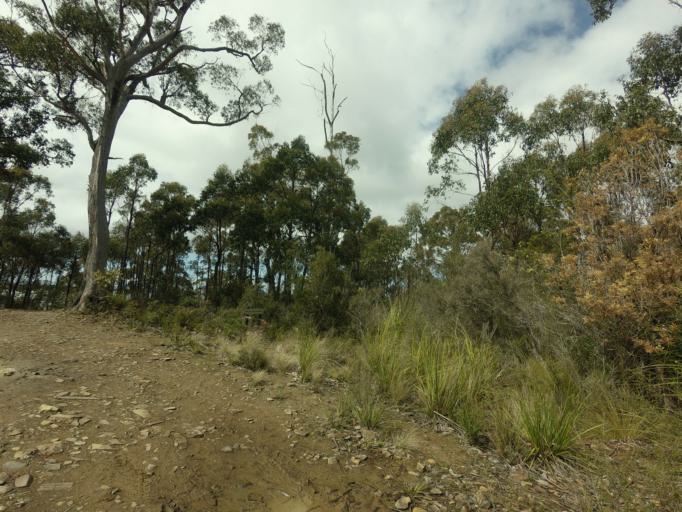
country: AU
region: Tasmania
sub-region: Huon Valley
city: Geeveston
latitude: -43.4817
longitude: 146.9384
